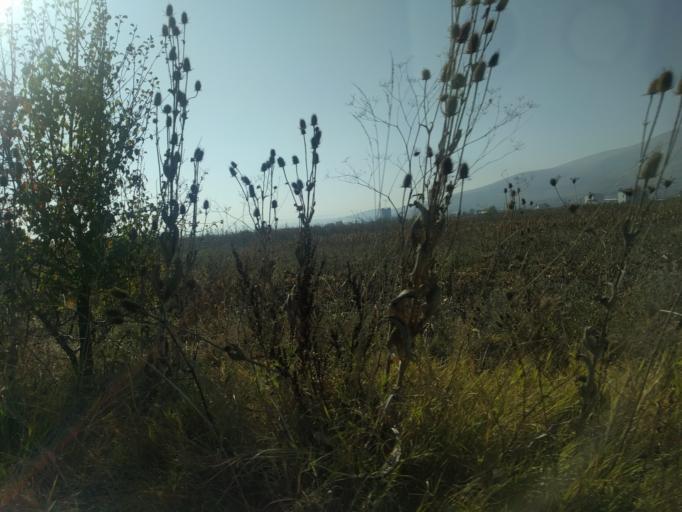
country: XK
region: Pristina
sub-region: Komuna e Gracanices
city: Glanica
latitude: 42.5869
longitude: 21.0183
